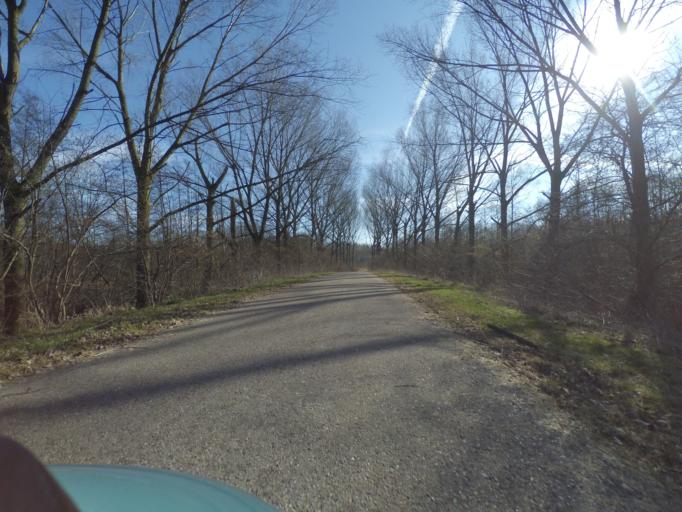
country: NL
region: Flevoland
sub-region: Gemeente Almere
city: Almere Stad
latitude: 52.4105
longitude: 5.2844
